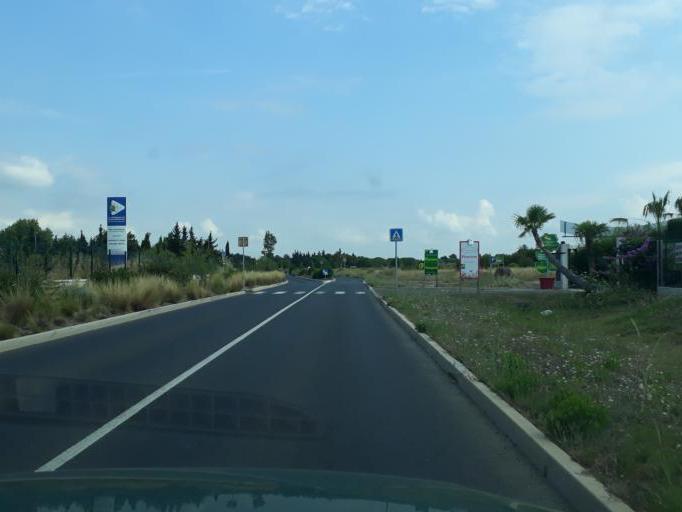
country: FR
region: Languedoc-Roussillon
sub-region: Departement de l'Herault
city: Agde
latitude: 43.2893
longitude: 3.4815
